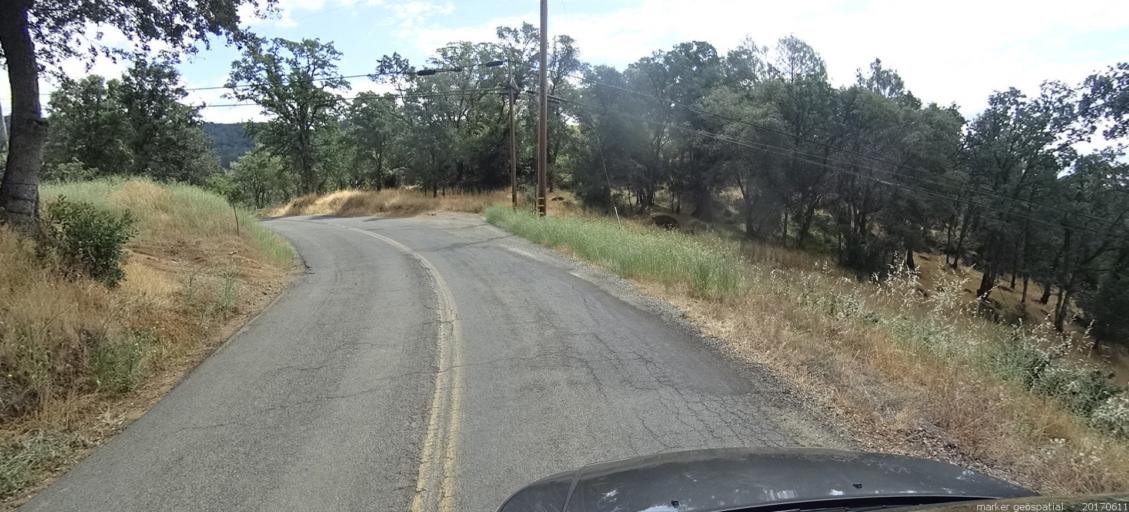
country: US
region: California
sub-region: Butte County
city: Oroville
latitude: 39.5485
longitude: -121.5416
